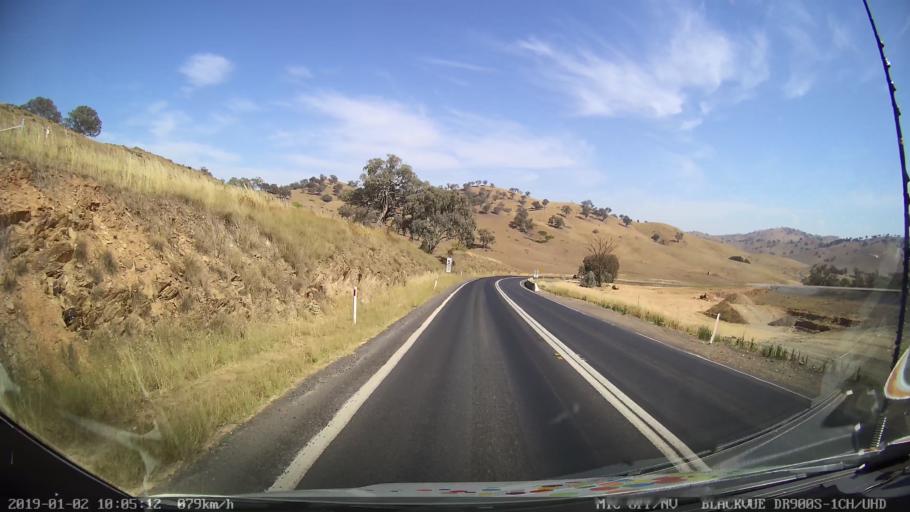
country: AU
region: New South Wales
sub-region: Gundagai
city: Gundagai
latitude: -35.1611
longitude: 148.1178
